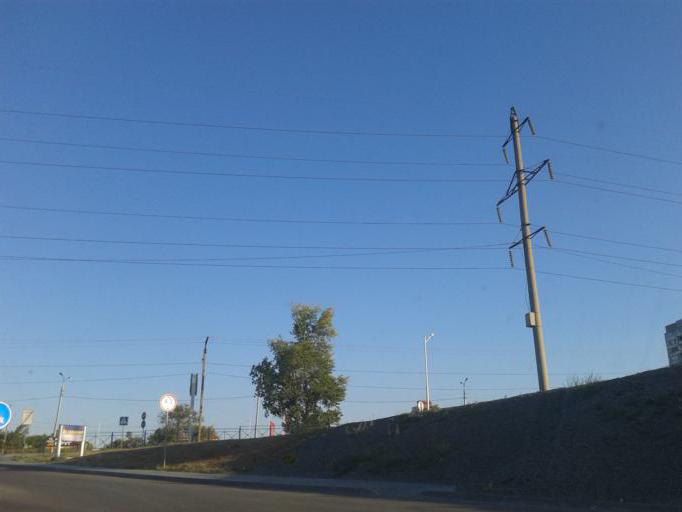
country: RU
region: Volgograd
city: Volgograd
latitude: 48.7628
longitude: 44.5082
